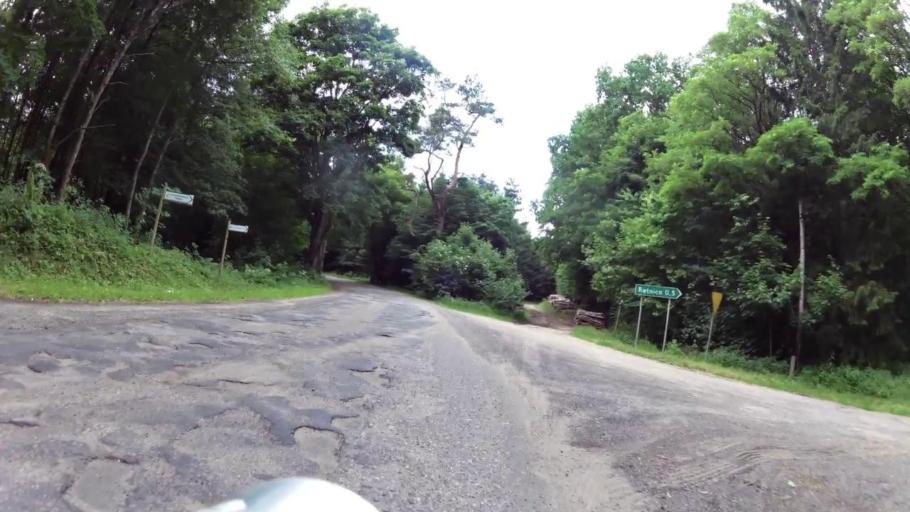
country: PL
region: West Pomeranian Voivodeship
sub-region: Powiat szczecinecki
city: Bialy Bor
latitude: 53.9652
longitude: 16.7272
